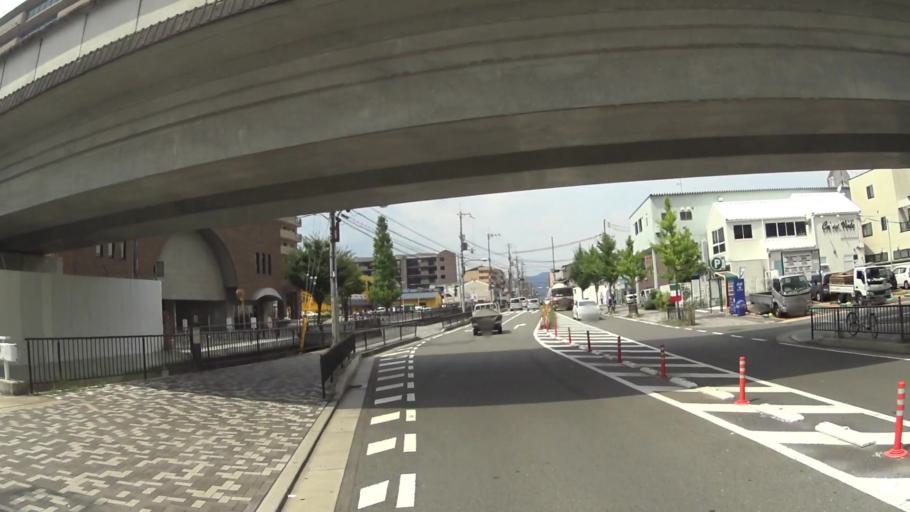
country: JP
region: Kyoto
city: Kyoto
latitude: 35.0090
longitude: 135.7415
